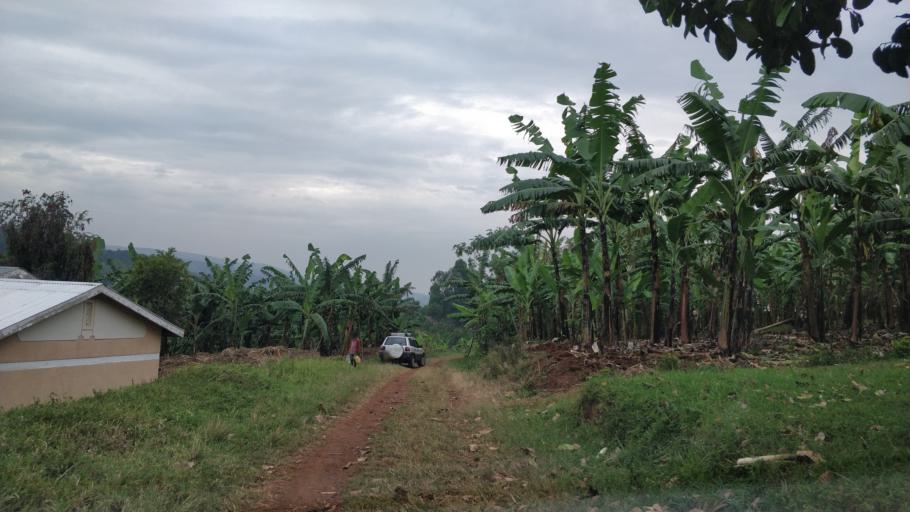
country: UG
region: Western Region
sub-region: Sheema District
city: Kibingo
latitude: -0.7029
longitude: 30.3992
